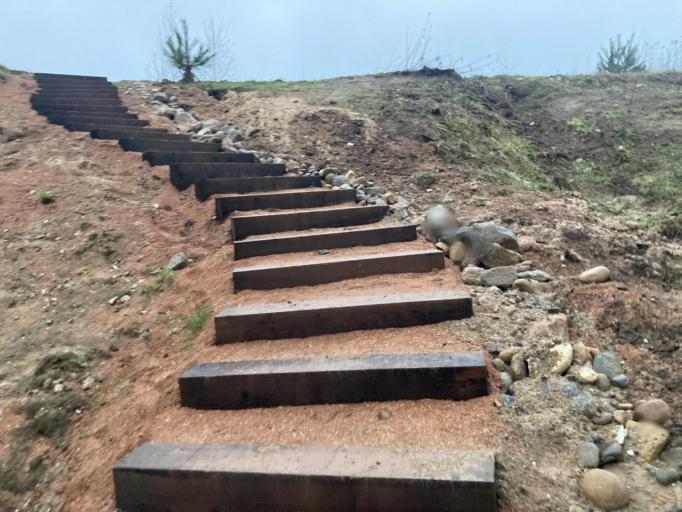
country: DK
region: Capital Region
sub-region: Hoje-Taastrup Kommune
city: Flong
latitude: 55.6785
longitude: 12.2335
